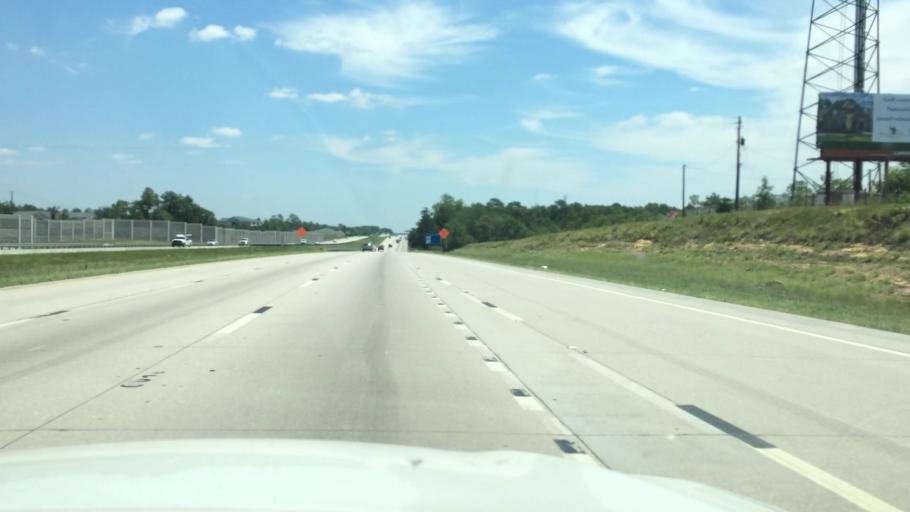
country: US
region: South Carolina
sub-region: Richland County
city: Woodfield
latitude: 34.0964
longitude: -80.8515
